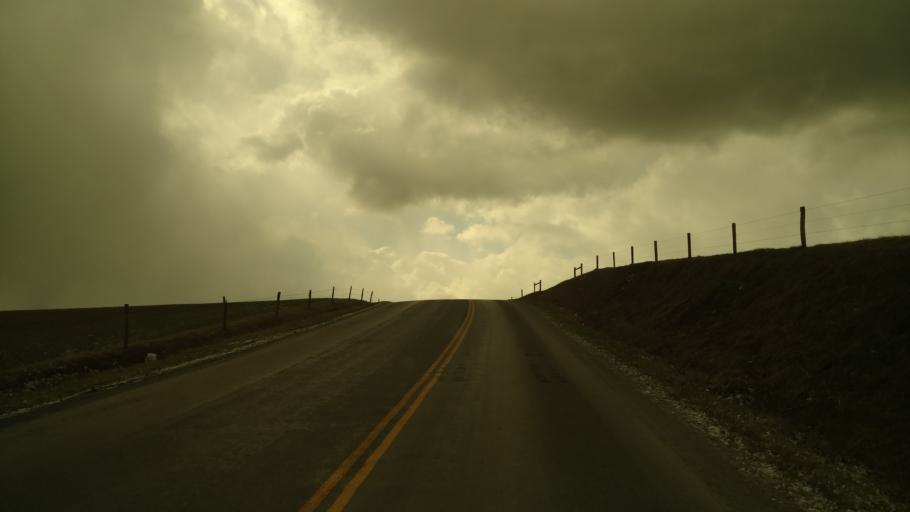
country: US
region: Ohio
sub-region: Tuscarawas County
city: Sugarcreek
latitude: 40.4731
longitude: -81.7808
